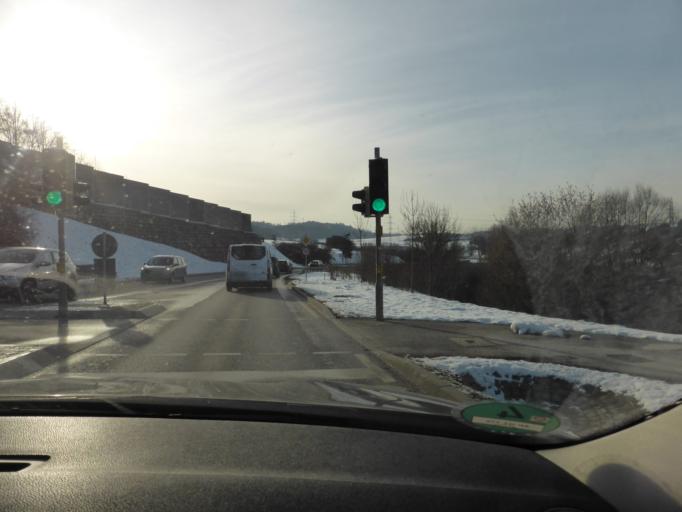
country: DE
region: Baden-Wuerttemberg
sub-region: Regierungsbezirk Stuttgart
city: Leonberg
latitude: 48.7937
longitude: 9.0002
